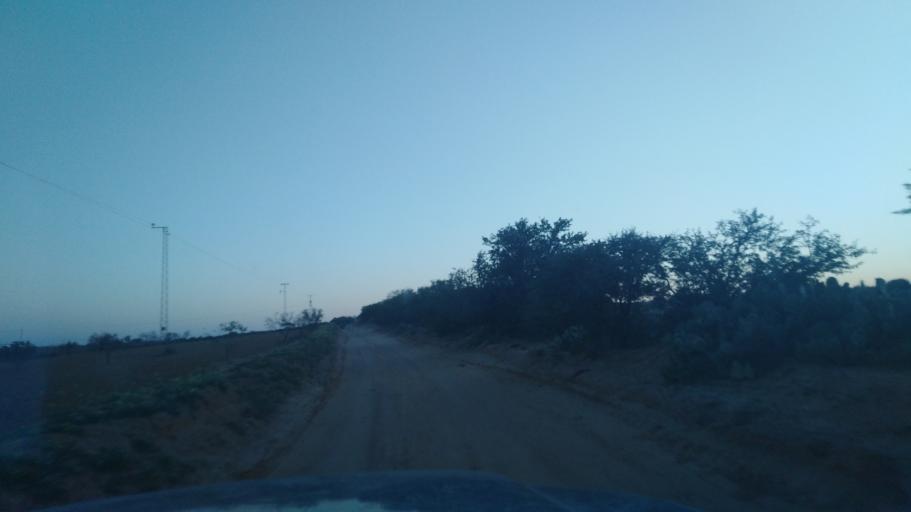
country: TN
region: Safaqis
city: Sfax
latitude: 34.7331
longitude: 10.4449
